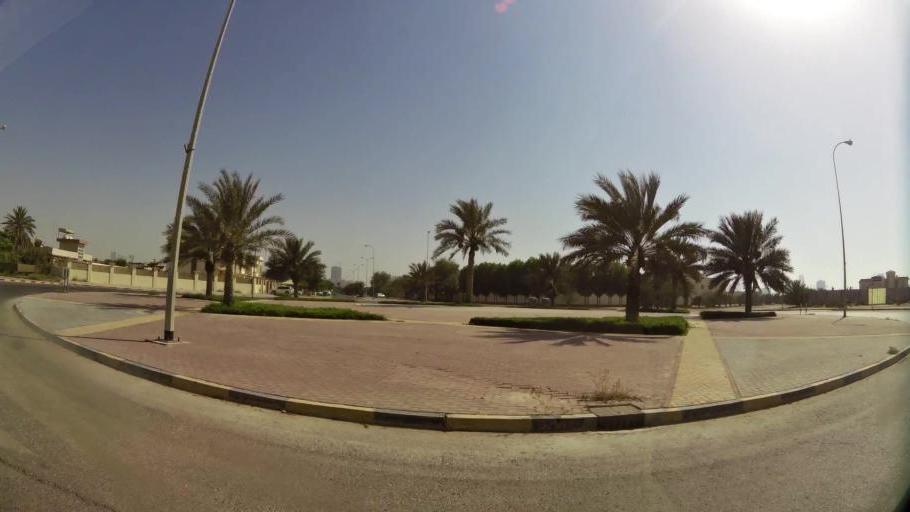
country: AE
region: Ajman
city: Ajman
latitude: 25.4124
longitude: 55.4676
